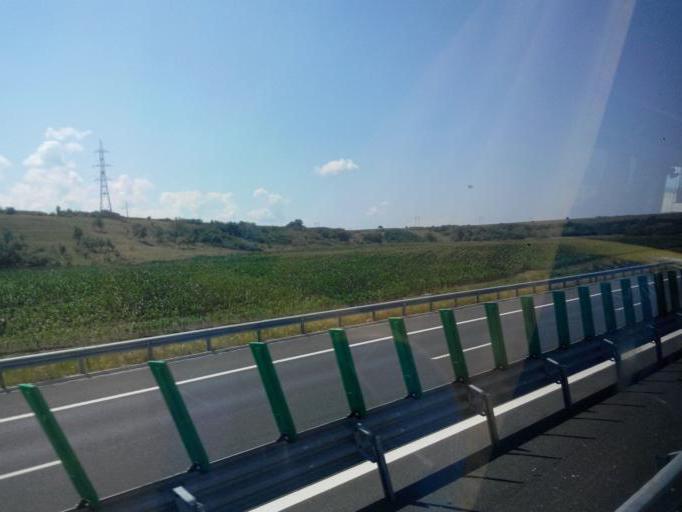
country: RO
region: Alba
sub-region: Comuna Saliste
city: Salistea
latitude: 45.9360
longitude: 23.3850
